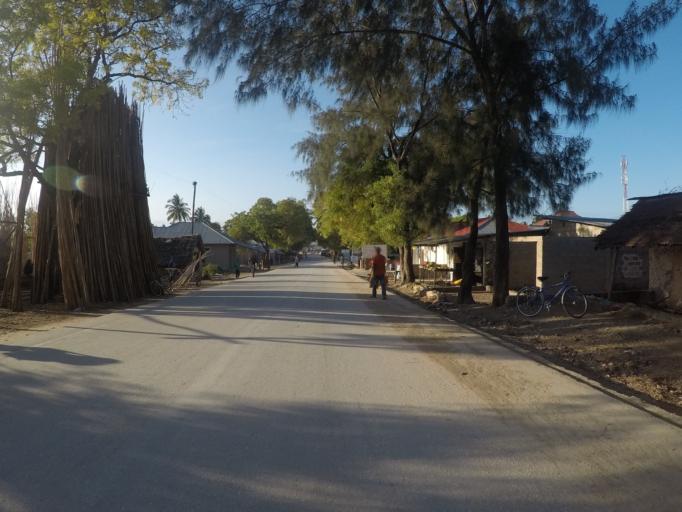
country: TZ
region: Zanzibar North
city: Nungwi
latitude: -5.7298
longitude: 39.2980
